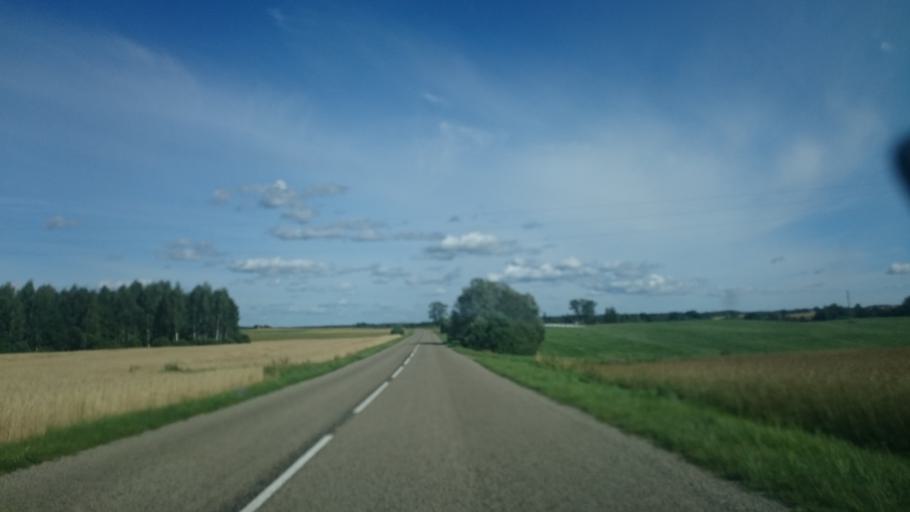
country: LV
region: Aizpute
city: Aizpute
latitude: 56.7031
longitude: 21.7758
